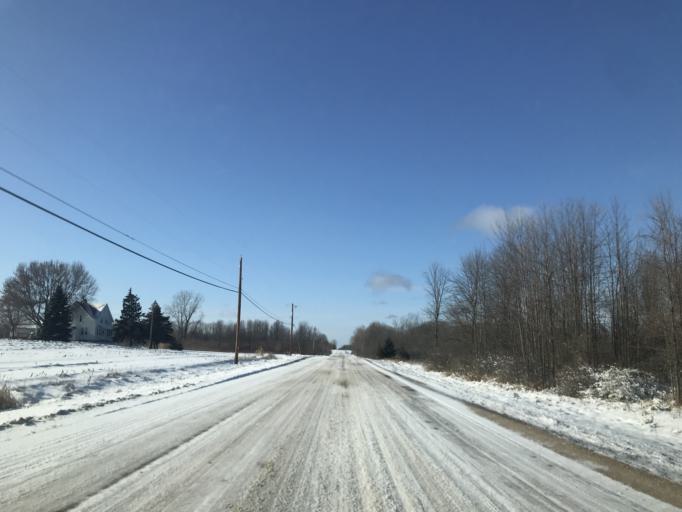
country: US
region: Wisconsin
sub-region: Door County
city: Sturgeon Bay
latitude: 44.8499
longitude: -87.4695
